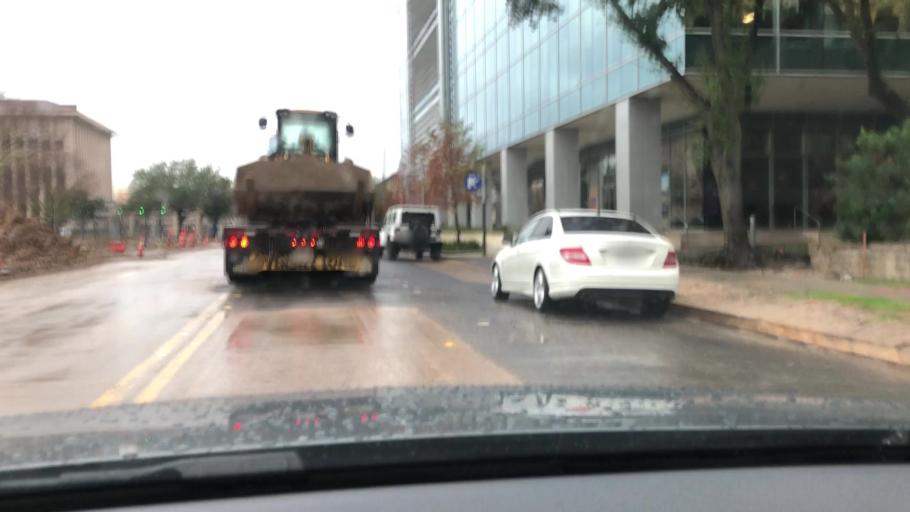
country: US
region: Texas
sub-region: Harris County
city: Bunker Hill Village
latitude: 29.7821
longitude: -95.5602
